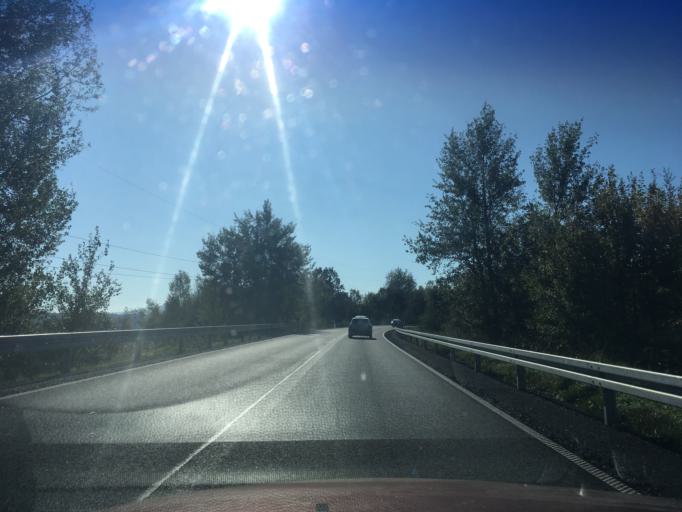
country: DE
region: Saxony
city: Hirschfelde
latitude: 50.9218
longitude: 14.8730
